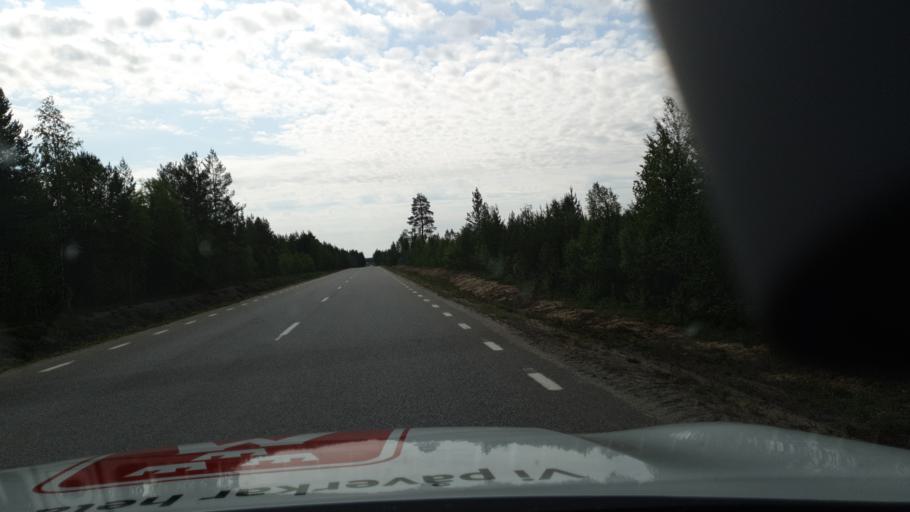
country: SE
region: Vaesterbotten
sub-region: Norsjo Kommun
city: Norsjoe
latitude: 64.5532
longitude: 19.3257
